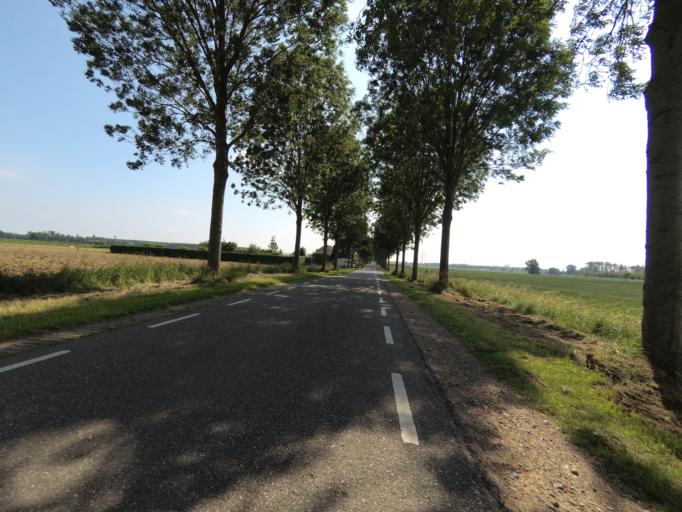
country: NL
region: Gelderland
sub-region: Gemeente Culemborg
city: Culemborg
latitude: 51.9393
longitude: 5.1647
